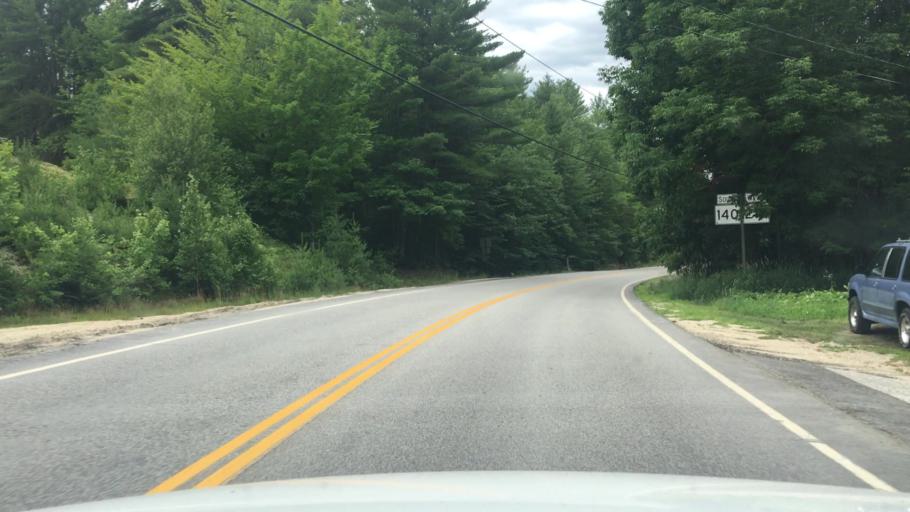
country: US
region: Maine
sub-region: Oxford County
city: Hartford
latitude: 44.3675
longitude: -70.3464
